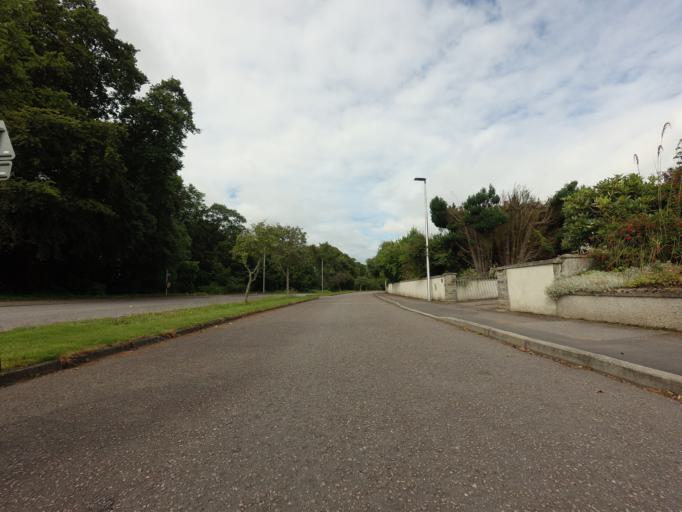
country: GB
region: Scotland
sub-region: Moray
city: Elgin
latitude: 57.6525
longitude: -3.3334
